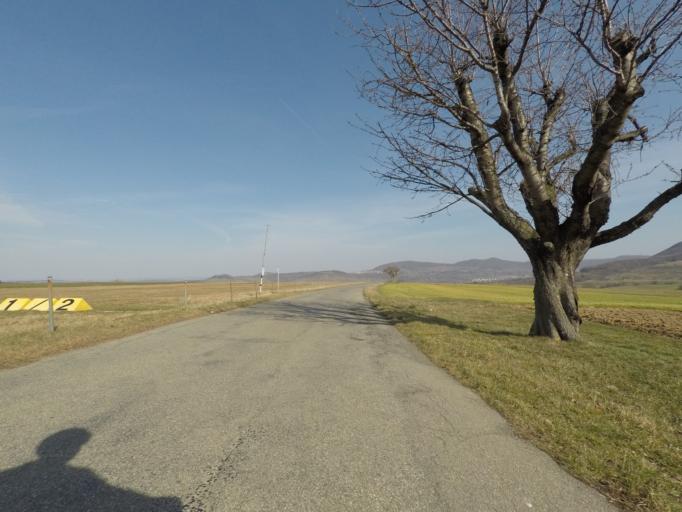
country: DE
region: Baden-Wuerttemberg
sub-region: Tuebingen Region
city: Metzingen
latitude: 48.5091
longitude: 9.2922
